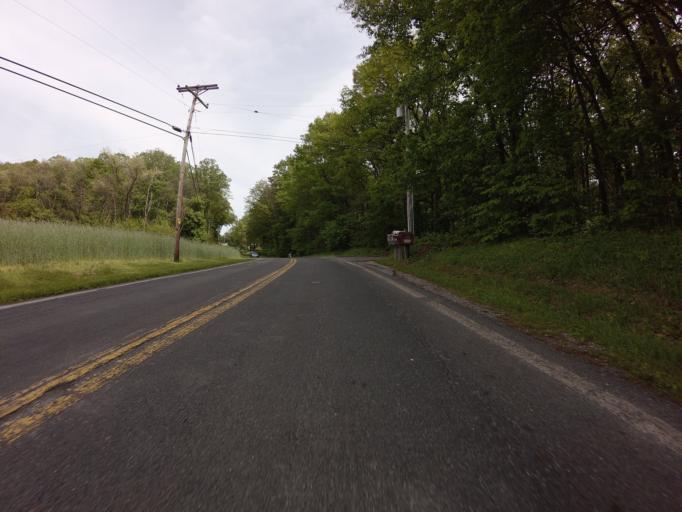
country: US
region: Maryland
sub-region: Carroll County
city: New Windsor
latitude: 39.4612
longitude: -77.0643
